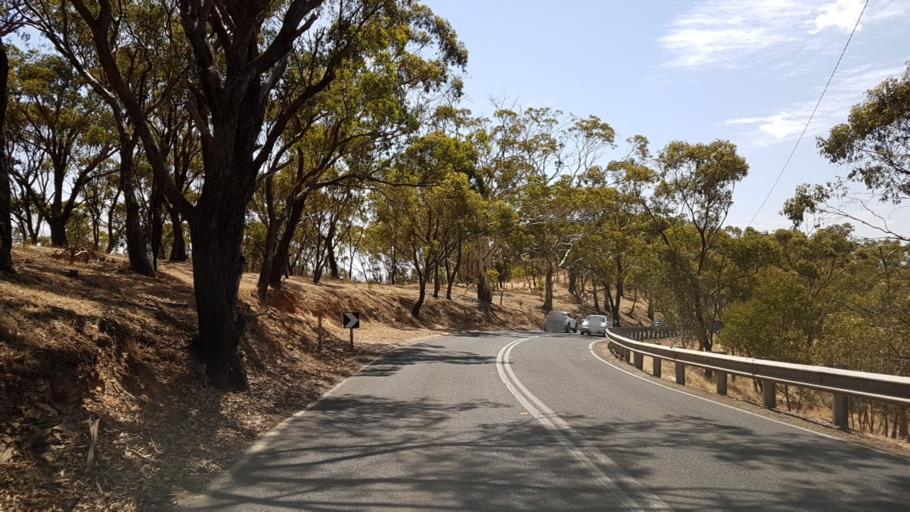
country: AU
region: South Australia
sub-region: Mitcham
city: Belair
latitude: -34.9918
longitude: 138.6251
